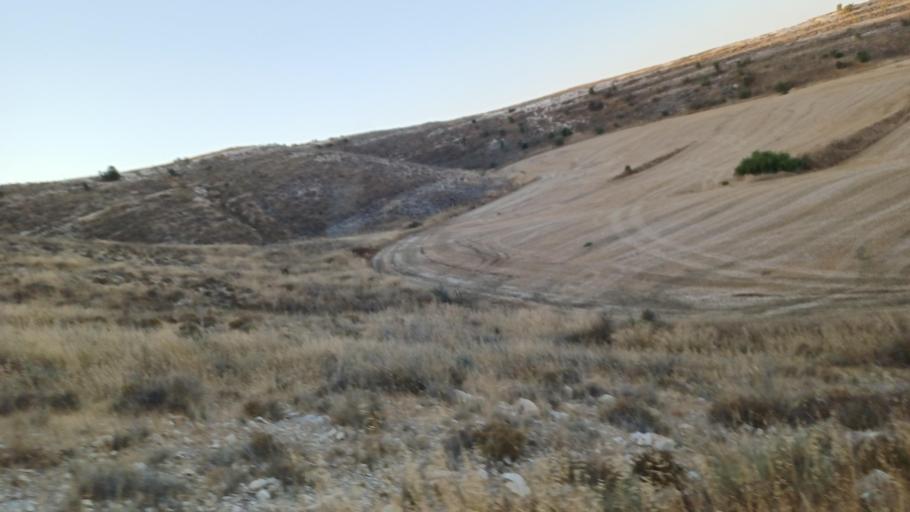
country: CY
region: Larnaka
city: Athienou
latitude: 35.0358
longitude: 33.4989
